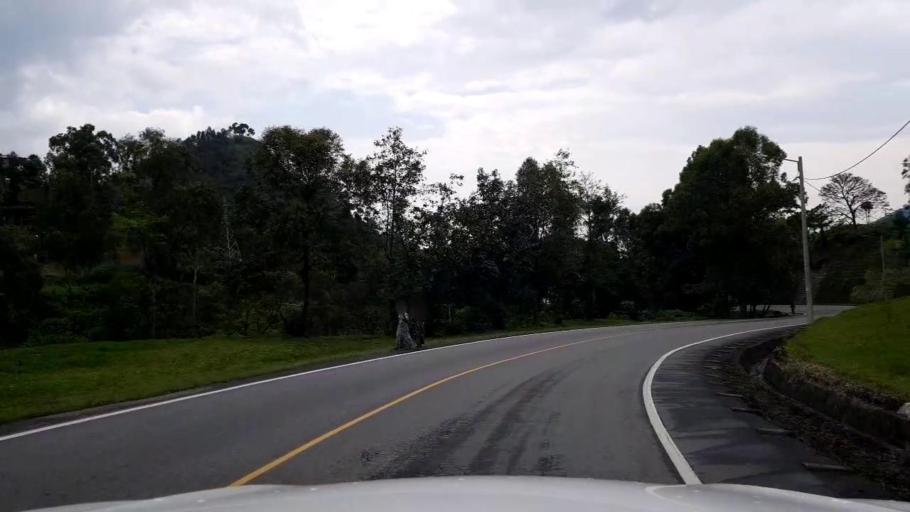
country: RW
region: Western Province
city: Gisenyi
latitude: -1.7023
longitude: 29.2716
